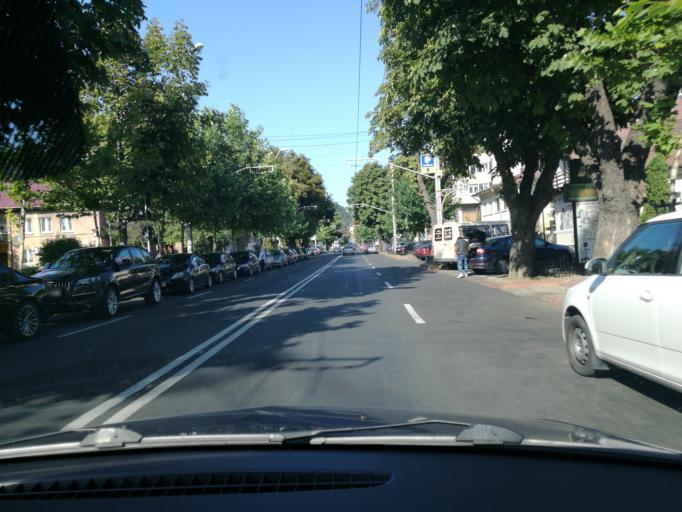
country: RO
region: Neamt
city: Piatra Neamt
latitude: 46.9283
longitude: 26.3621
